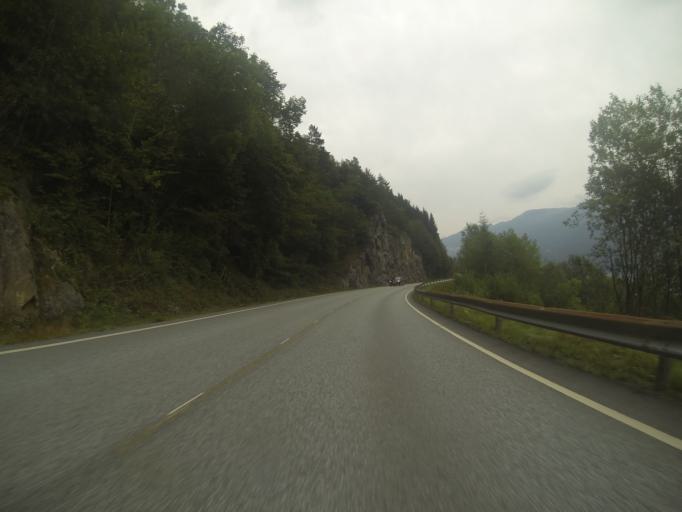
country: NO
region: Rogaland
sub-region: Suldal
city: Sand
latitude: 59.5676
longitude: 6.2752
